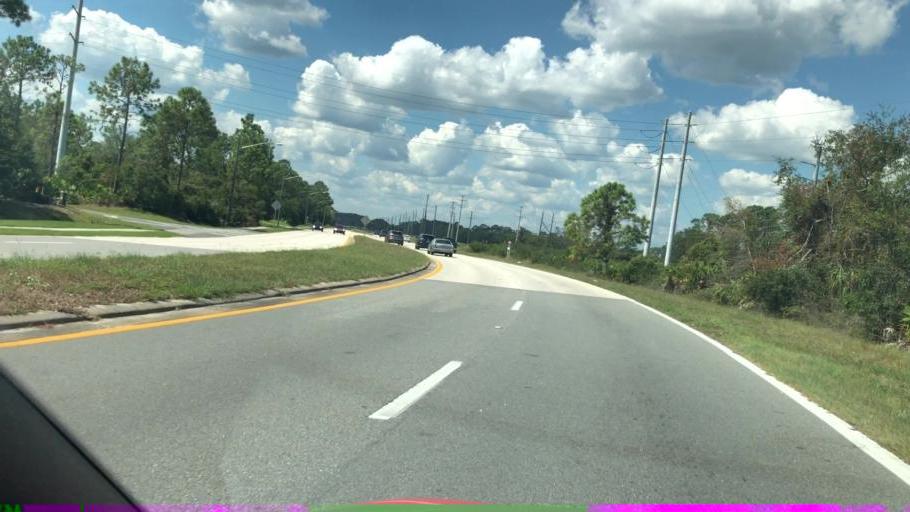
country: US
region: Florida
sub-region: Volusia County
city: Holly Hill
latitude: 29.2150
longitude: -81.0633
